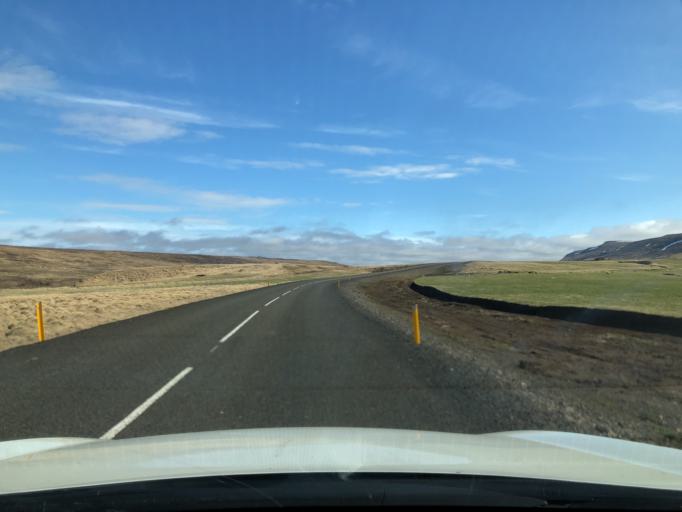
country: IS
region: West
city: Borgarnes
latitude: 65.1450
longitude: -21.5888
